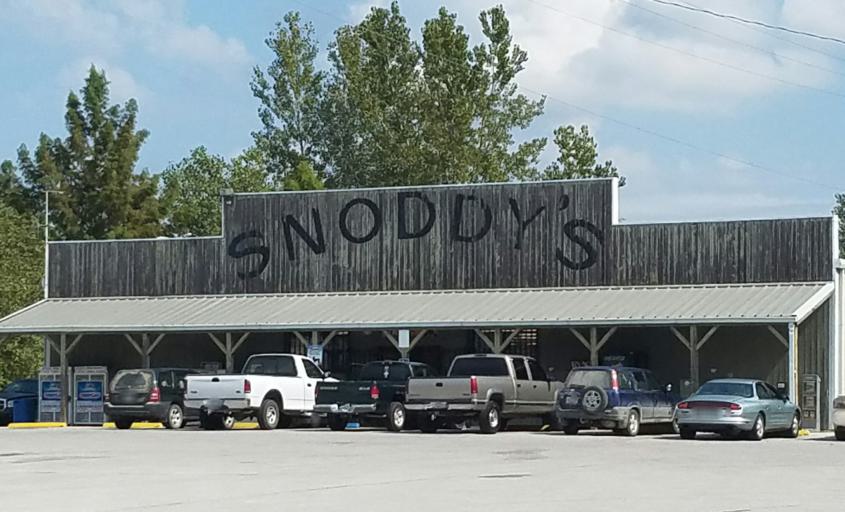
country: US
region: Missouri
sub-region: Cooper County
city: Boonville
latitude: 38.9894
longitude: -92.7464
